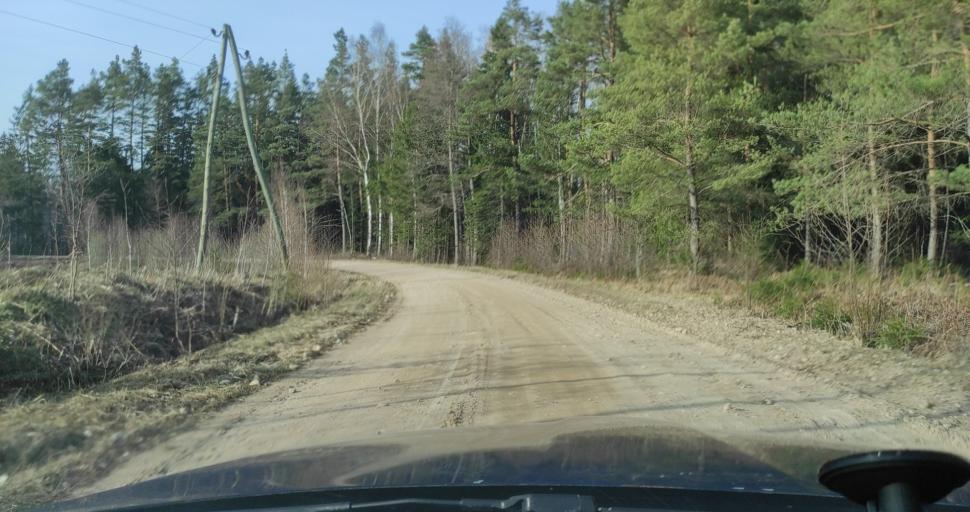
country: LV
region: Kuldigas Rajons
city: Kuldiga
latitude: 57.0163
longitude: 22.0138
